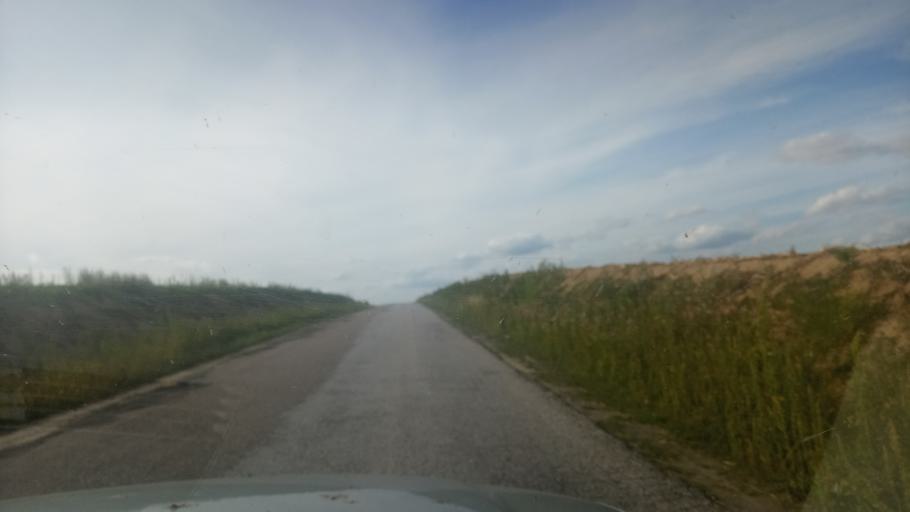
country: PL
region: Kujawsko-Pomorskie
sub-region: Powiat nakielski
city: Sadki
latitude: 53.1978
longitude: 17.3847
